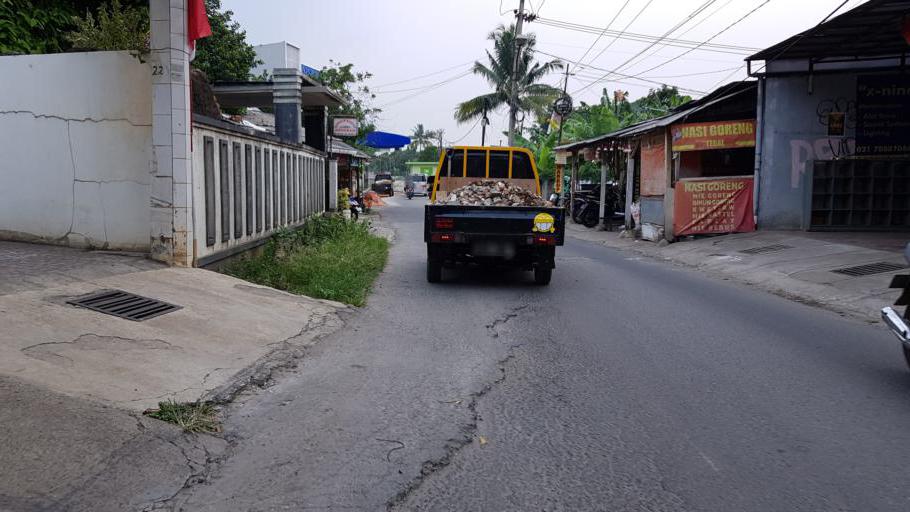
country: ID
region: West Java
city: Depok
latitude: -6.3693
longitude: 106.8163
